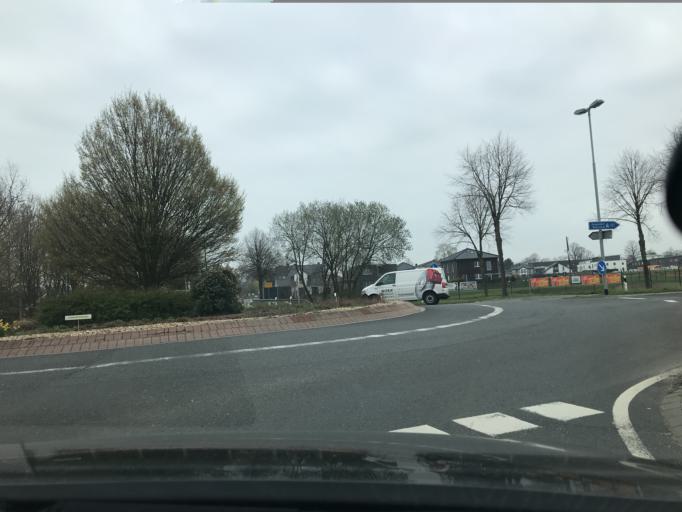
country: DE
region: North Rhine-Westphalia
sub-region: Regierungsbezirk Dusseldorf
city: Schwalmtal
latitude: 51.2131
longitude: 6.2624
